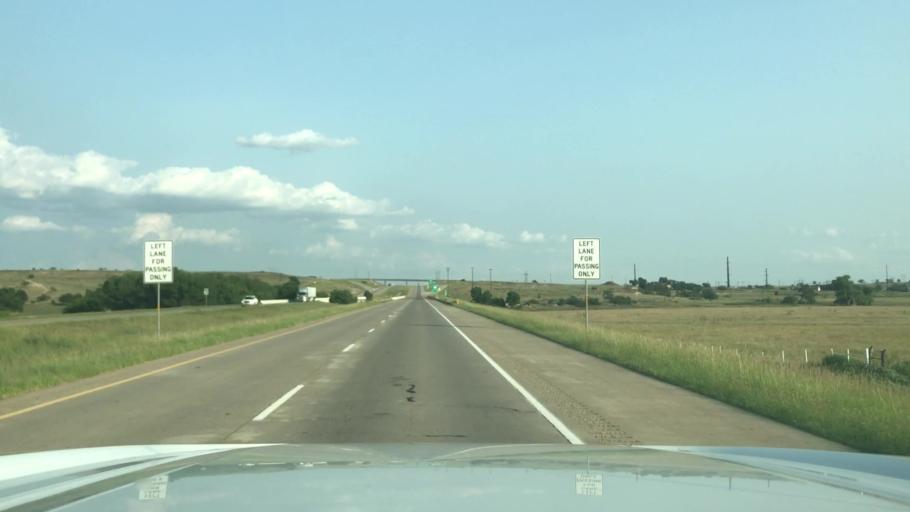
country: US
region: Texas
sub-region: Randall County
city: Canyon
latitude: 35.0073
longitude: -101.9047
